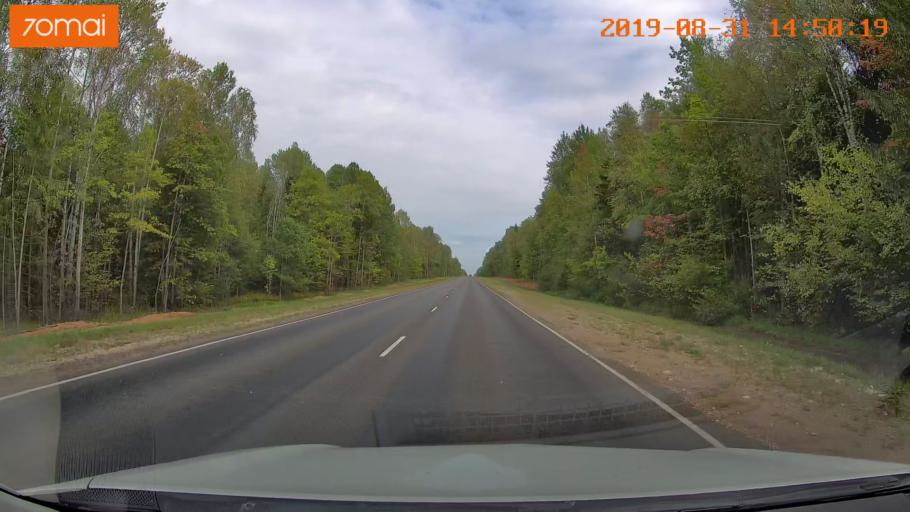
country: RU
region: Kaluga
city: Spas-Demensk
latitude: 54.2604
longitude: 33.7865
